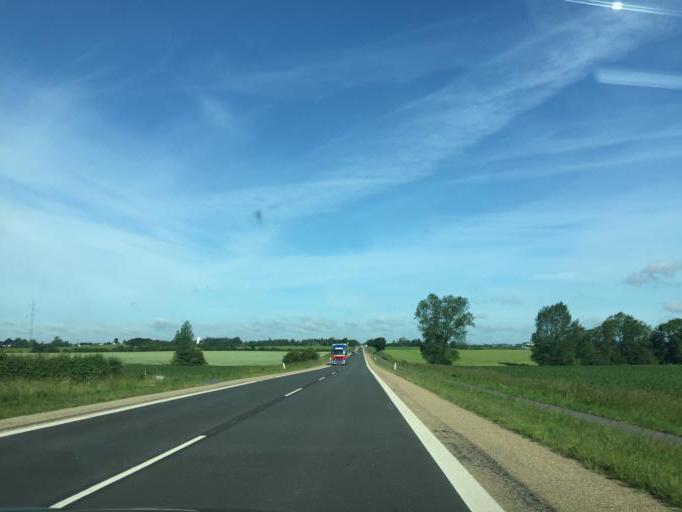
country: DK
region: South Denmark
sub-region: Middelfart Kommune
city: Norre Aby
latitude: 55.4835
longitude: 9.8304
